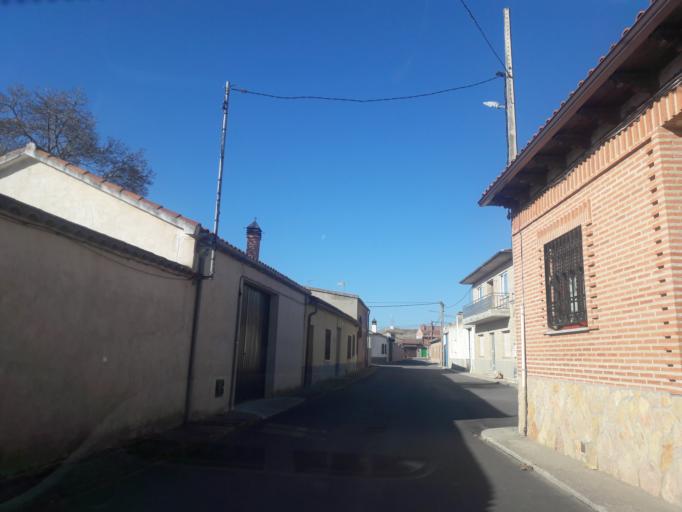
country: ES
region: Castille and Leon
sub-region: Provincia de Salamanca
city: Penarandilla
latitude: 40.8837
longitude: -5.3935
